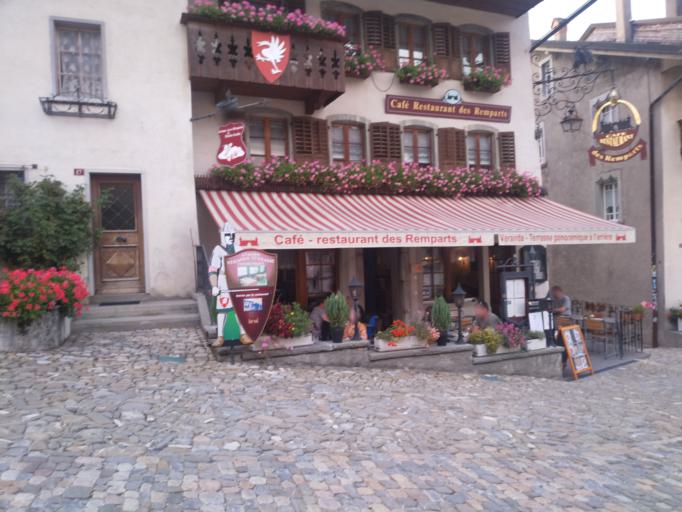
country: CH
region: Fribourg
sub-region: Gruyere District
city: Gruyeres
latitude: 46.5834
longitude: 7.0810
